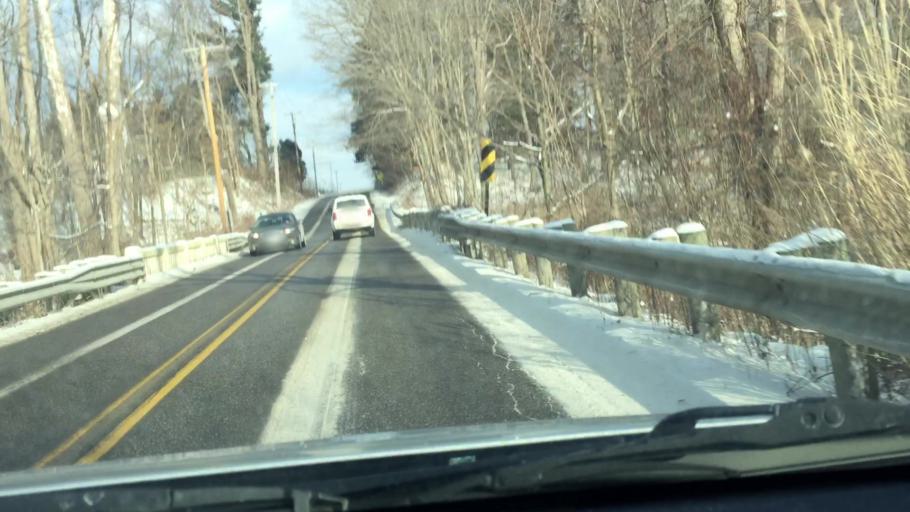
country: US
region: Ohio
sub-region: Mahoning County
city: Boardman
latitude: 41.0131
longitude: -80.7113
